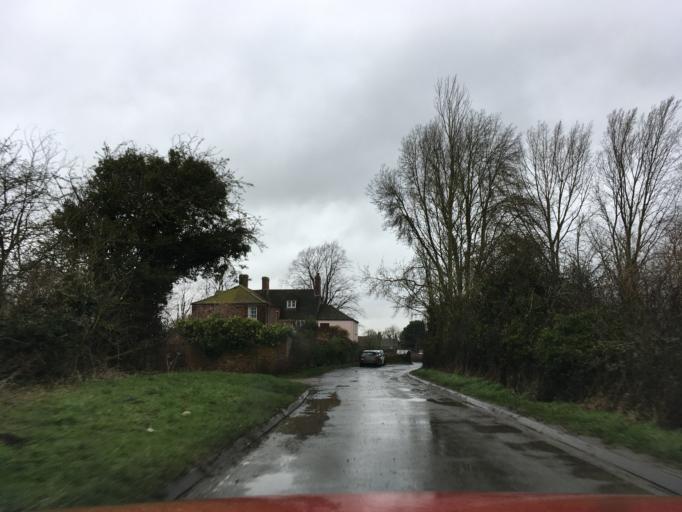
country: GB
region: England
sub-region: Oxfordshire
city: Oxford
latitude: 51.7637
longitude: -1.2871
